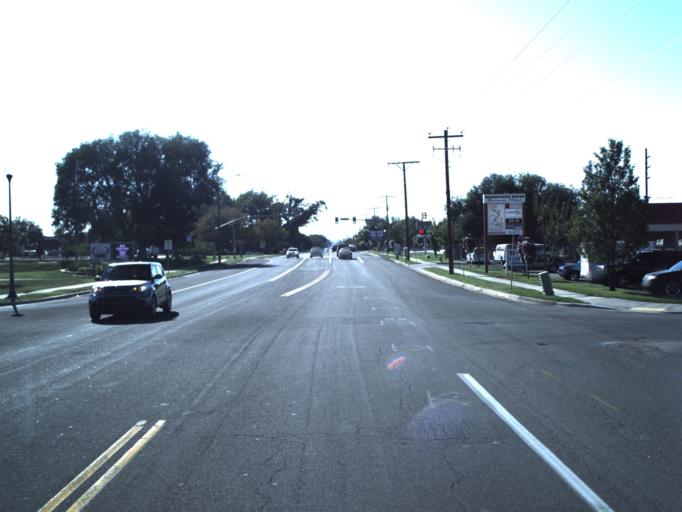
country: US
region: Utah
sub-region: Davis County
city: Clinton
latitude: 41.1399
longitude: -112.0436
